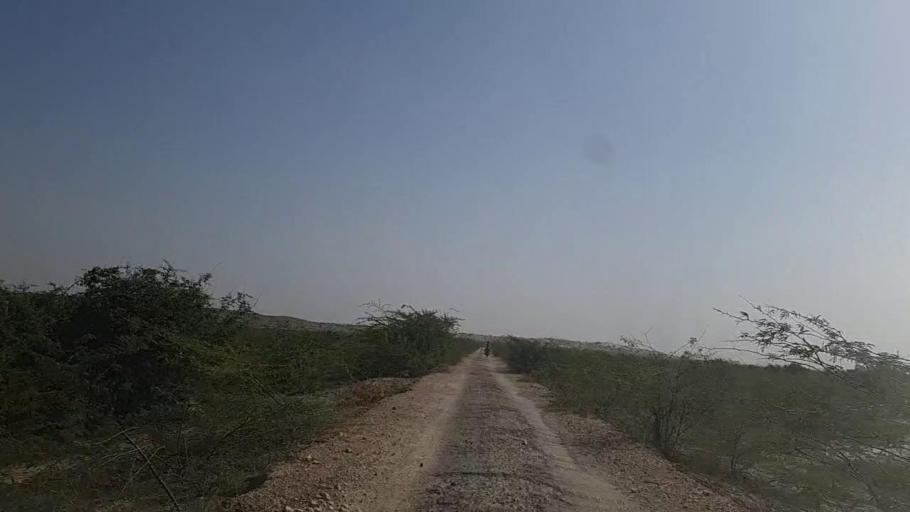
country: PK
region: Sindh
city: Naukot
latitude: 24.5851
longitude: 69.2929
